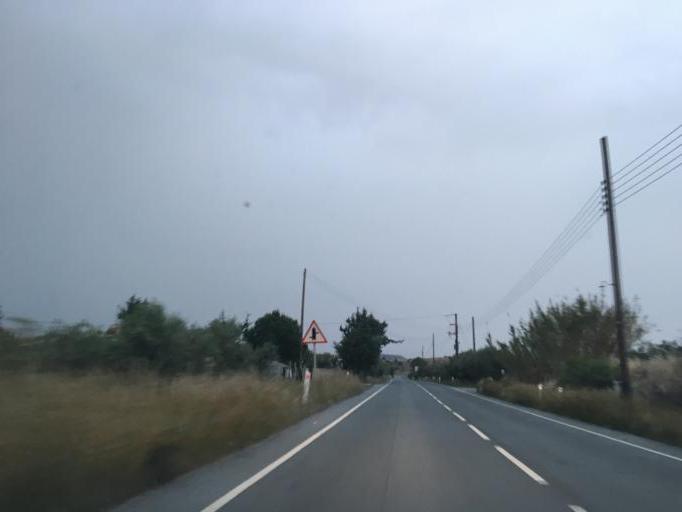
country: CY
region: Limassol
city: Parekklisha
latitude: 34.7701
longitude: 33.1629
